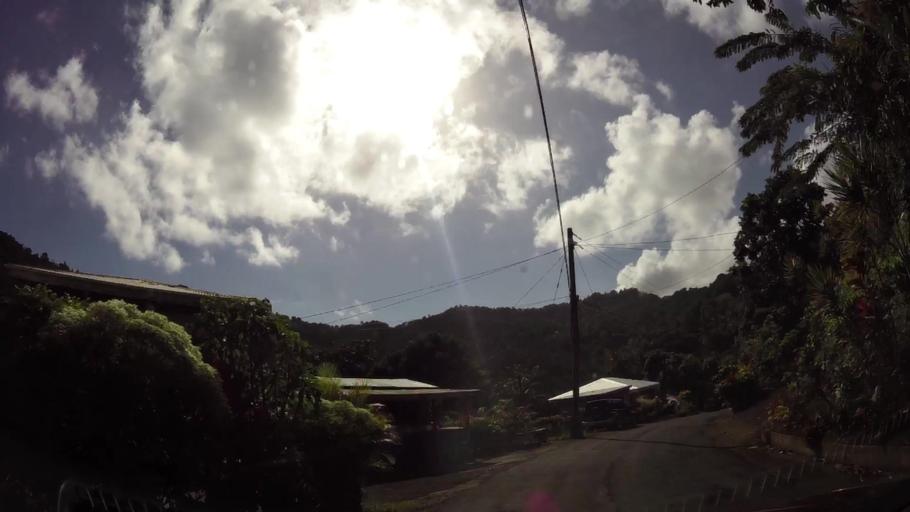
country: DM
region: Saint Andrew
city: Marigot
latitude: 15.5156
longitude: -61.2712
